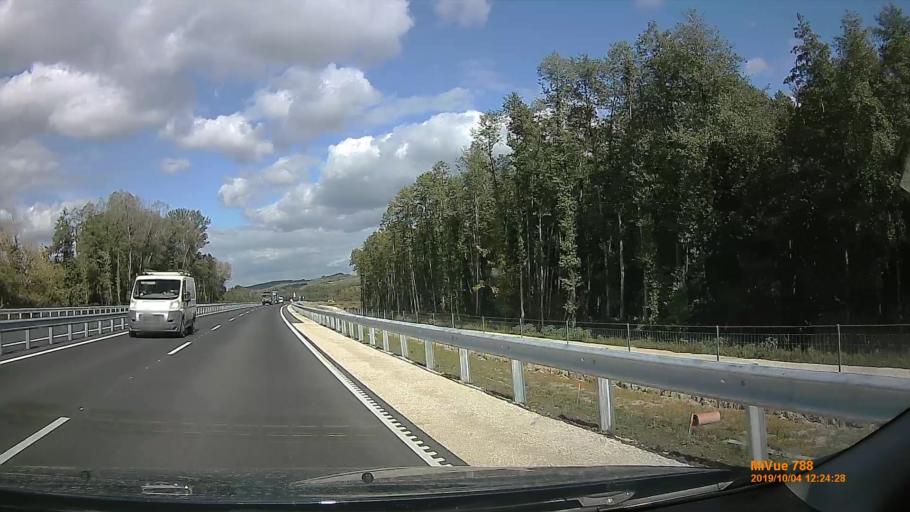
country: HU
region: Somogy
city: Karad
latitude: 46.6495
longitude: 17.7862
